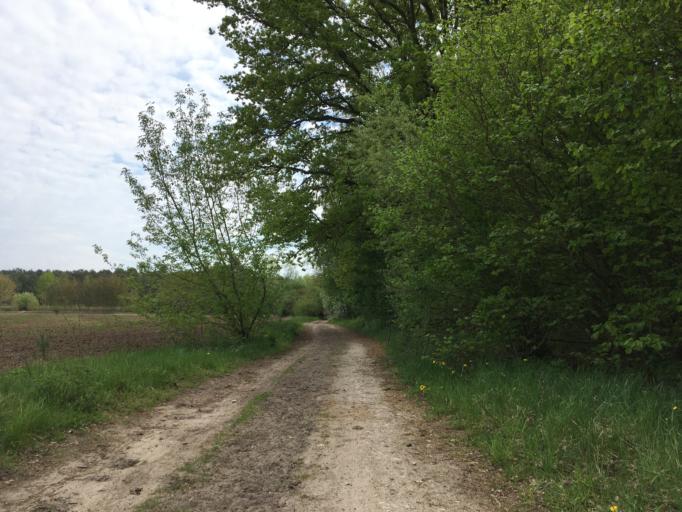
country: DE
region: Brandenburg
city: Rudnitz
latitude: 52.7118
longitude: 13.6260
